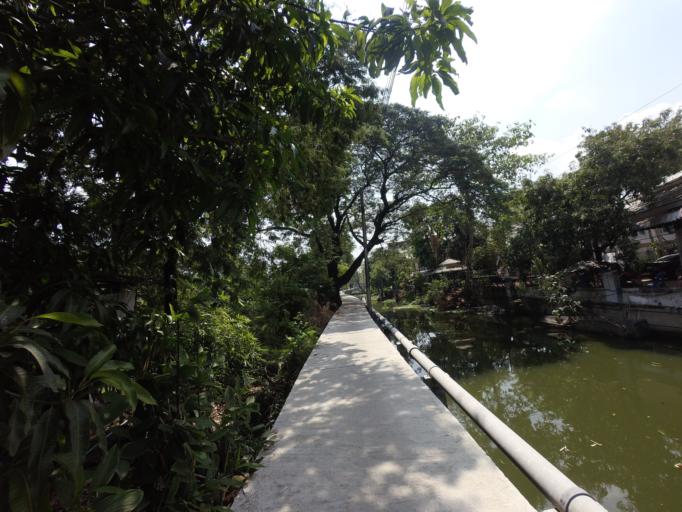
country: TH
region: Bangkok
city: Saphan Sung
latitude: 13.7597
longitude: 100.6695
